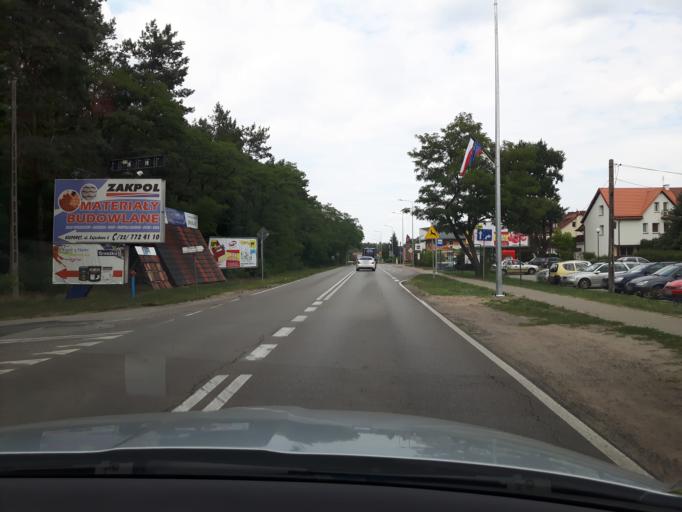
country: PL
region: Masovian Voivodeship
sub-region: Powiat legionowski
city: Nieporet
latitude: 52.4027
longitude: 21.0376
